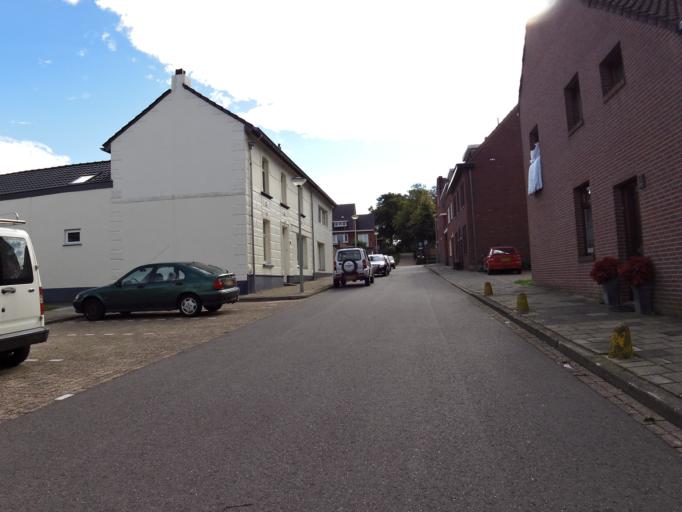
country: NL
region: Limburg
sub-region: Gemeente Heerlen
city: Nieuw-Lotbroek
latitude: 50.9167
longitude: 5.9580
